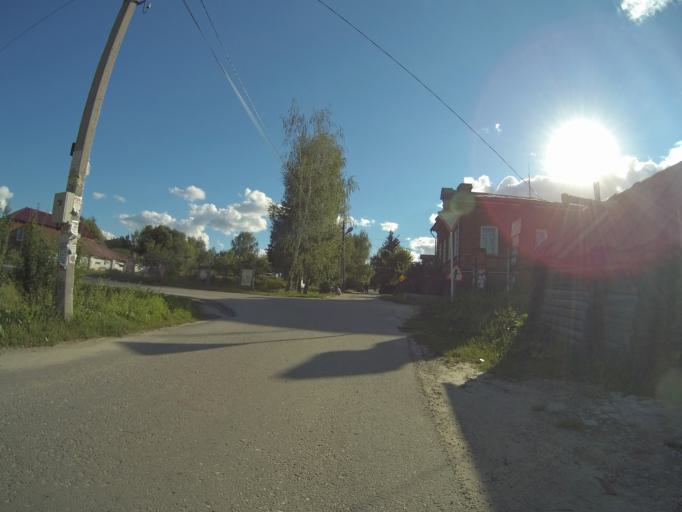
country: RU
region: Vladimir
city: Vladimir
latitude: 56.1776
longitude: 40.3659
